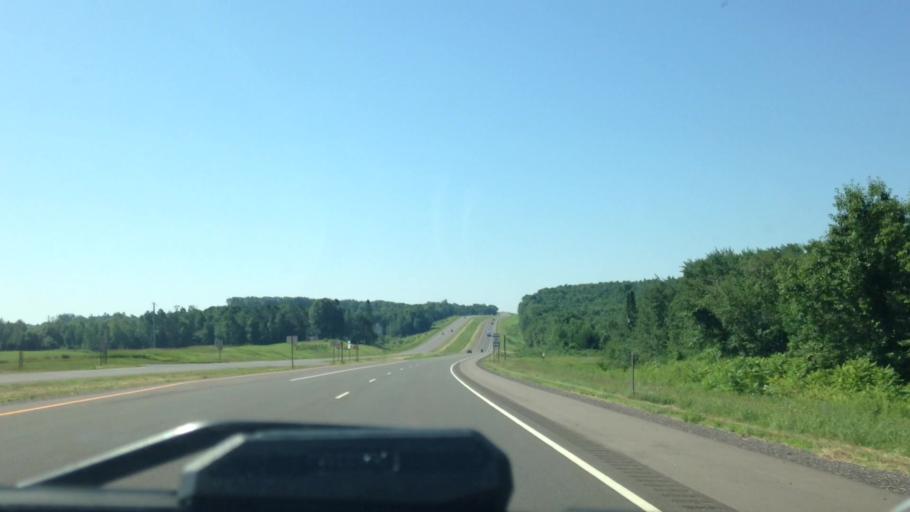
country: US
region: Wisconsin
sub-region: Washburn County
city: Spooner
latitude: 45.9820
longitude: -91.8278
